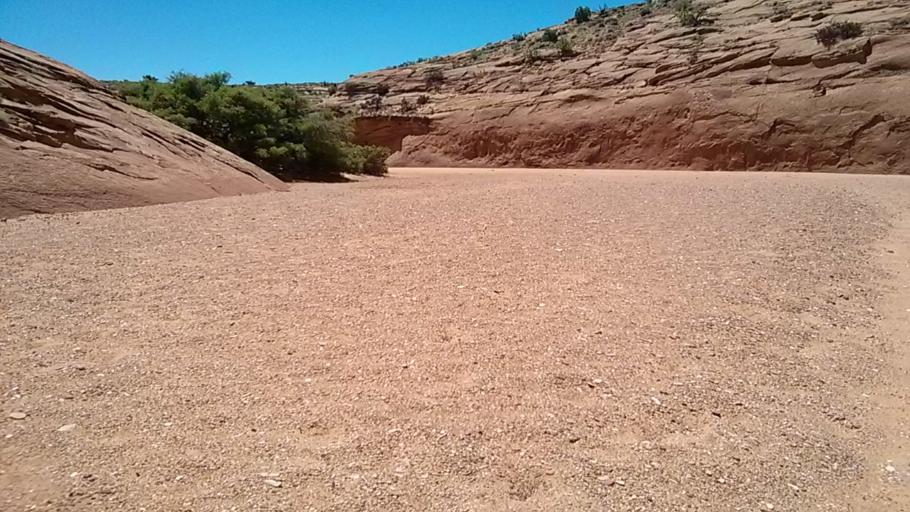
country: US
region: Arizona
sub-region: Coconino County
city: Page
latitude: 37.4813
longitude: -111.2094
